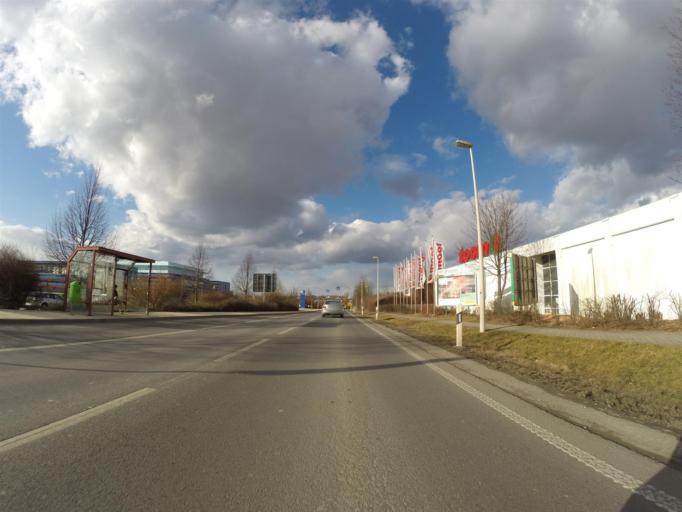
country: DE
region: Thuringia
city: Apolda
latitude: 51.0124
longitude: 11.5138
